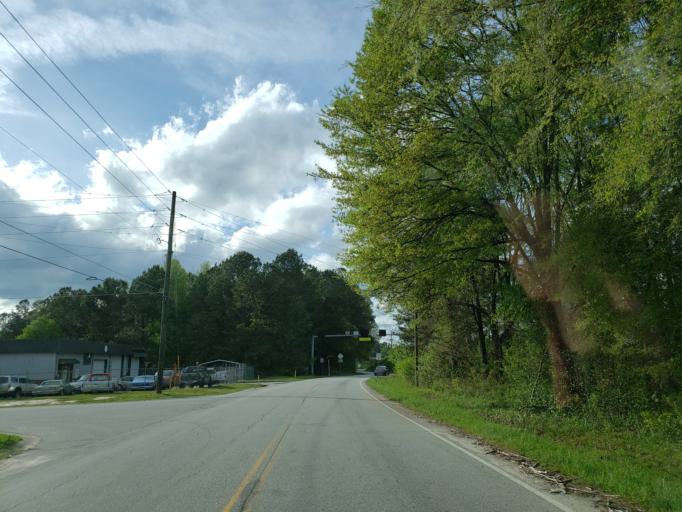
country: US
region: Georgia
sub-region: Paulding County
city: Hiram
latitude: 33.8805
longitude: -84.7448
